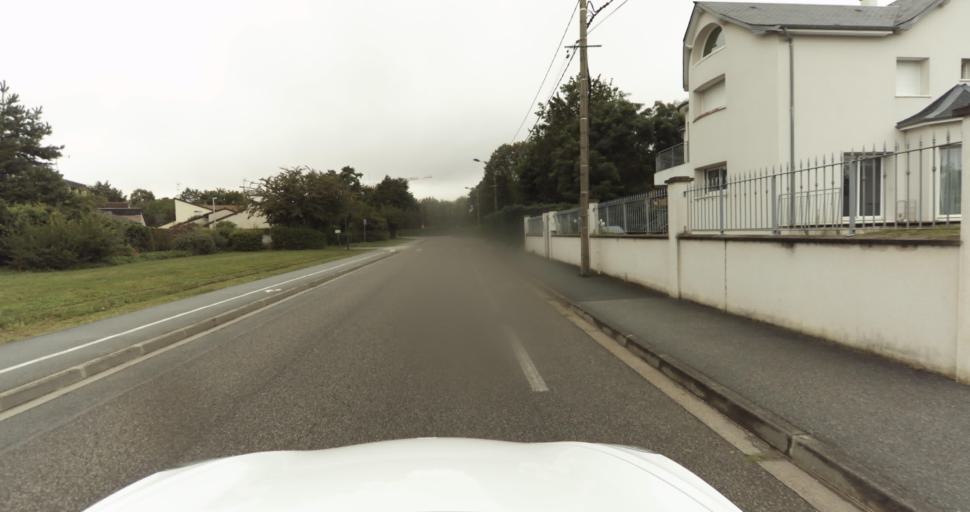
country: FR
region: Haute-Normandie
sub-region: Departement de l'Eure
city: Aviron
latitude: 49.0375
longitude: 1.1319
